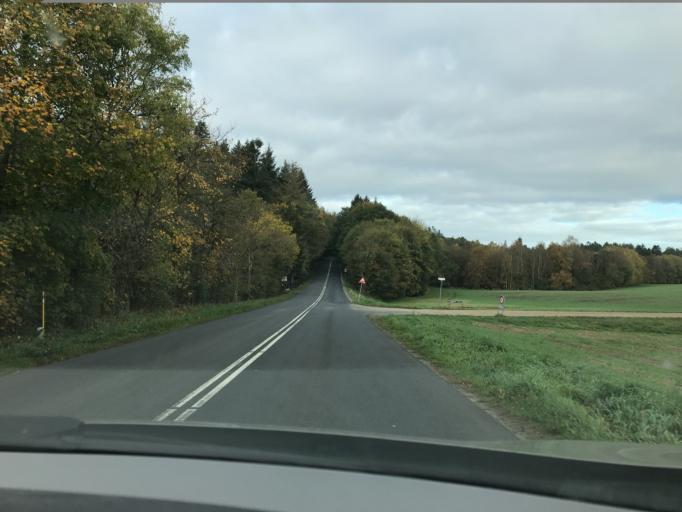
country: DK
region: South Denmark
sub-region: Kolding Kommune
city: Kolding
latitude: 55.5313
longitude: 9.4216
